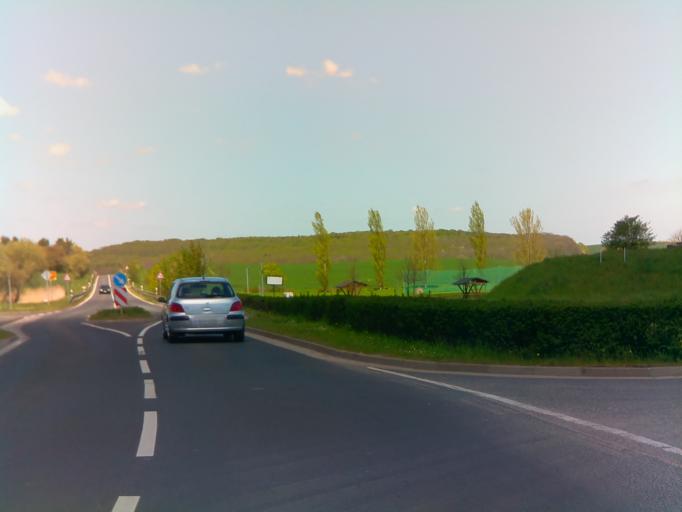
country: DE
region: Thuringia
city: Dornheim
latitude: 50.7977
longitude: 10.9824
